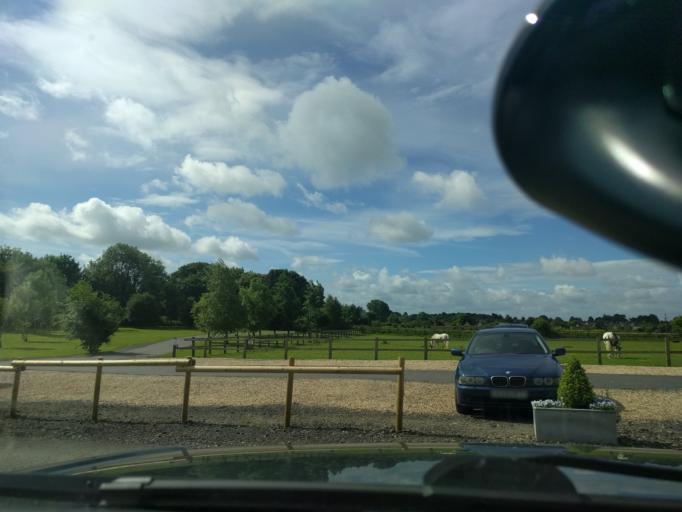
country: GB
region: England
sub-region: Bath and North East Somerset
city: Freshford
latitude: 51.3547
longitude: -2.2864
